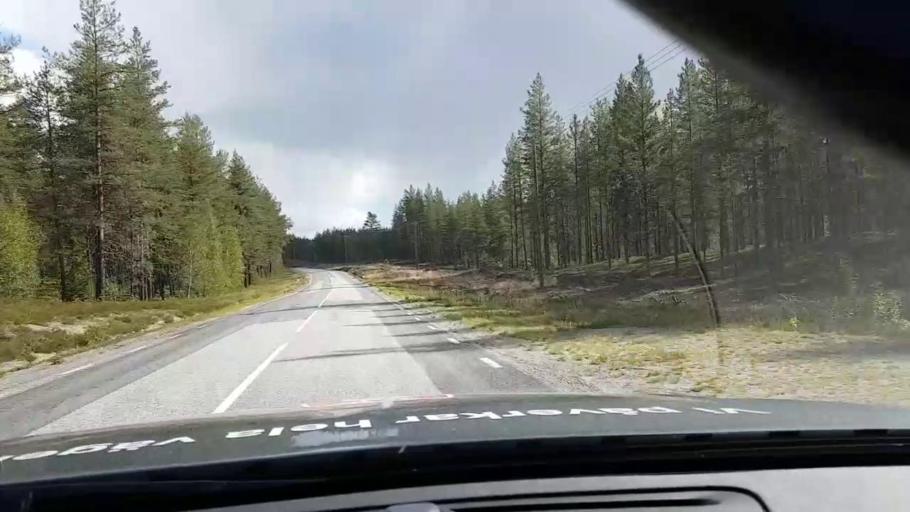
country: SE
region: Vaesterbotten
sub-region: Asele Kommun
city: Asele
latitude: 63.8556
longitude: 17.3874
